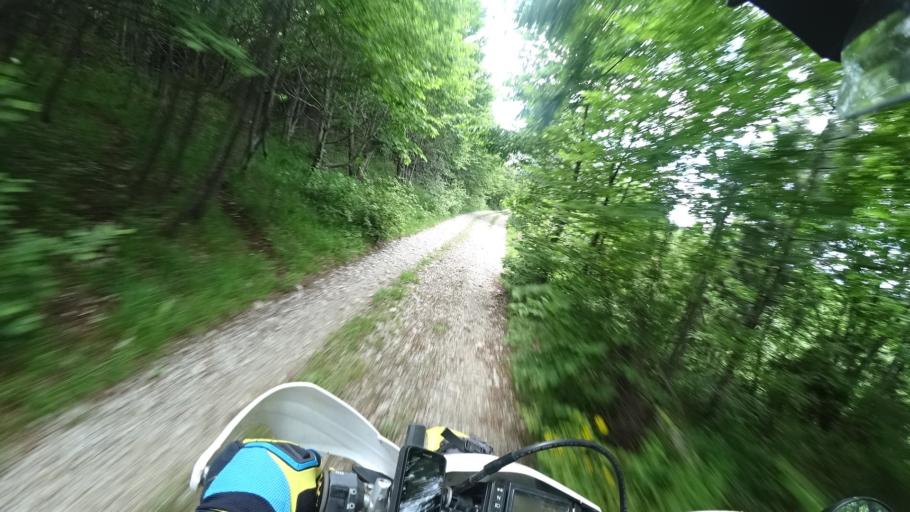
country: HR
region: Primorsko-Goranska
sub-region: Grad Crikvenica
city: Jadranovo
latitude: 45.2495
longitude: 14.6773
